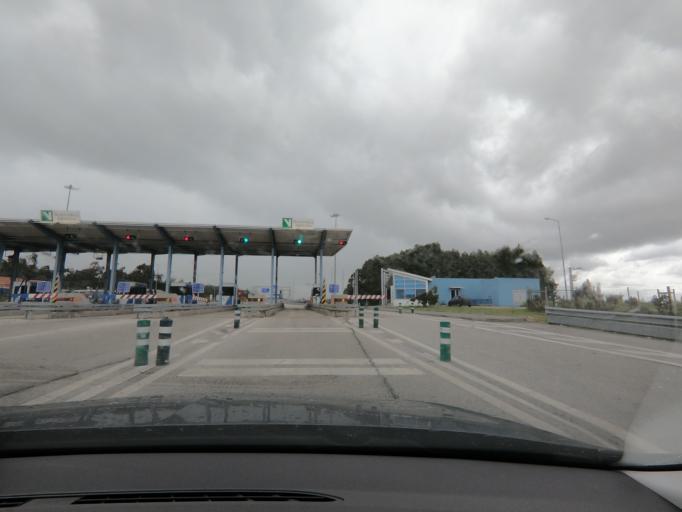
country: PT
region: Lisbon
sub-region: Sintra
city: Sintra
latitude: 38.7782
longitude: -9.3642
